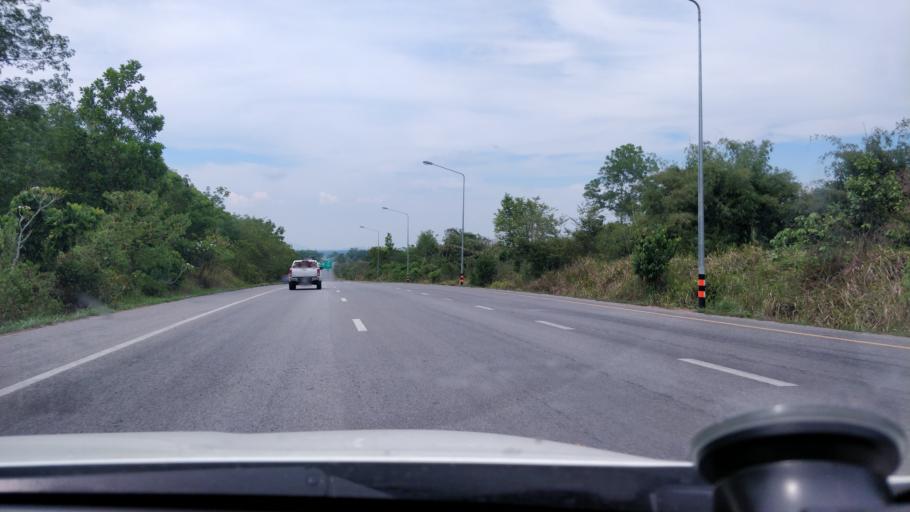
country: TH
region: Surat Thani
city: Khian Sa
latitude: 8.8156
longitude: 99.1677
